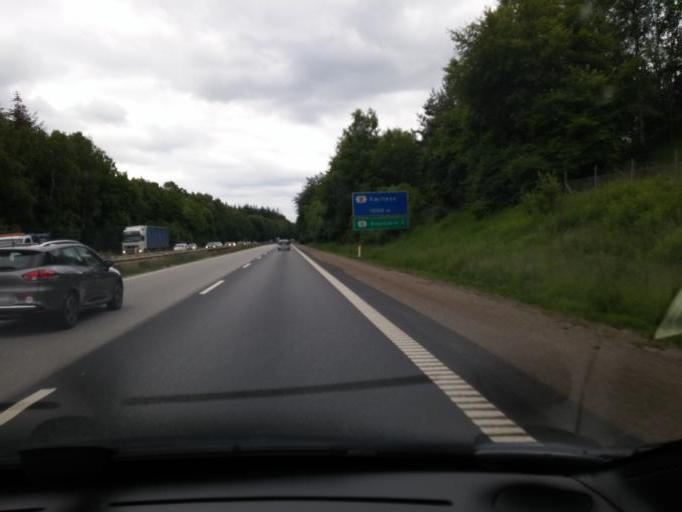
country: DK
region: Capital Region
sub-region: Fureso Kommune
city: Vaerlose
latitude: 55.7913
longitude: 12.3844
